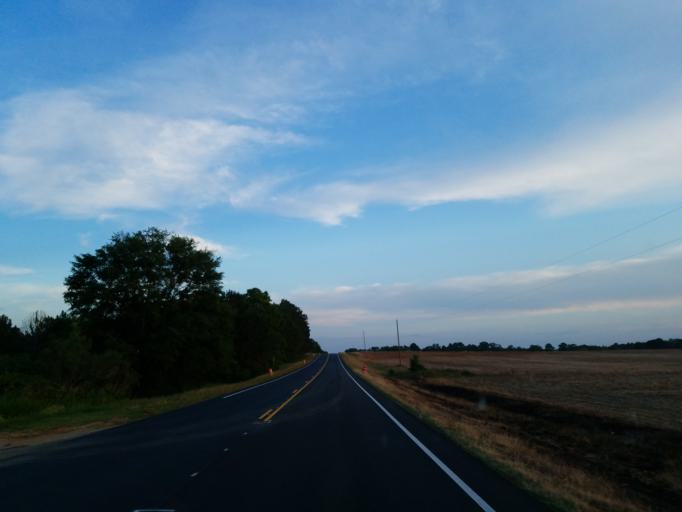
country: US
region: Georgia
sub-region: Turner County
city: Ashburn
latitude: 31.7859
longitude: -83.8056
